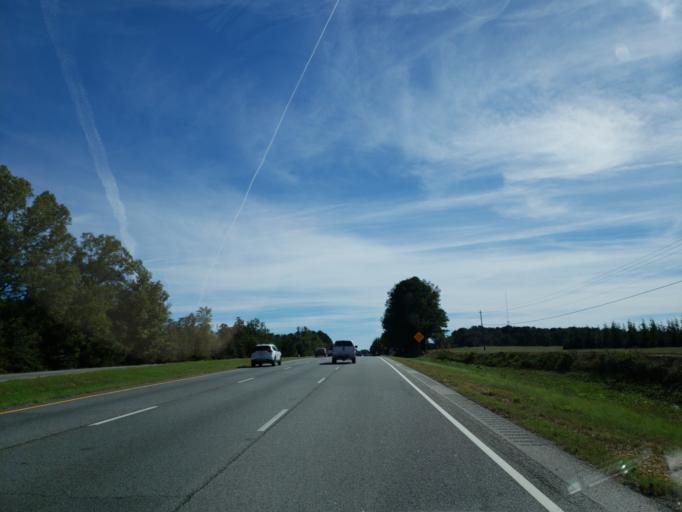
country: US
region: Georgia
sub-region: Henry County
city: Hampton
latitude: 33.3575
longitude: -84.2964
